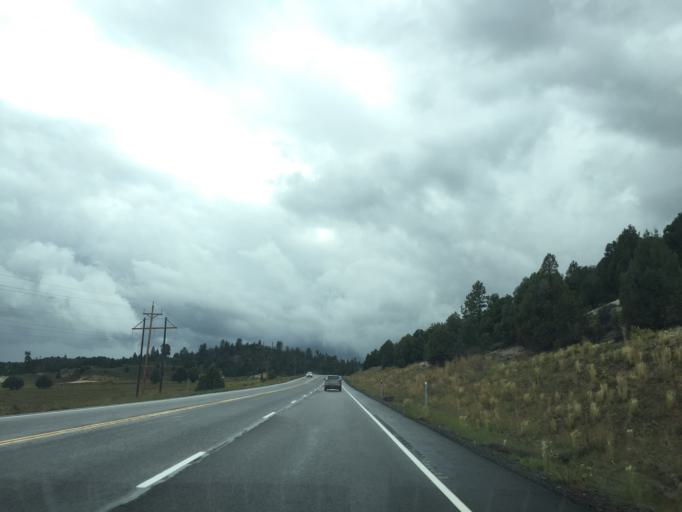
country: US
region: Utah
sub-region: Garfield County
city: Panguitch
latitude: 37.5026
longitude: -112.5013
